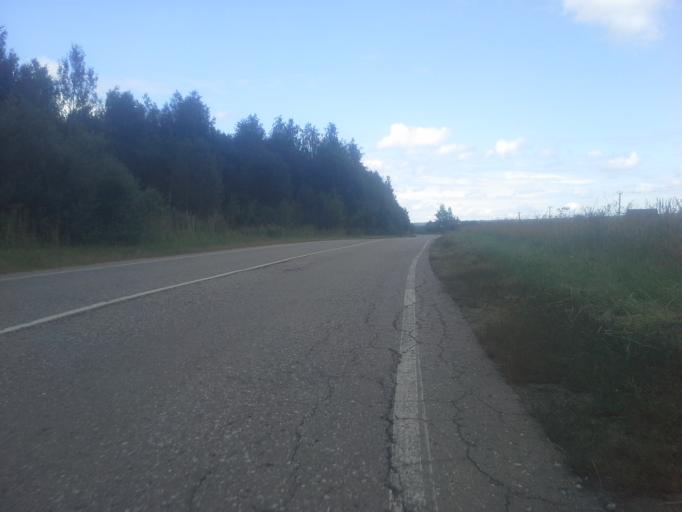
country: RU
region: Moskovskaya
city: Kolyubakino
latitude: 55.6479
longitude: 36.5744
